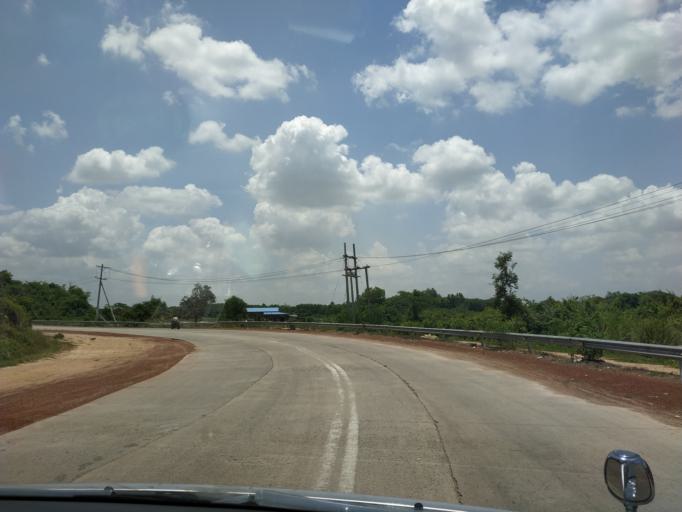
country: MM
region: Bago
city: Bago
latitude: 17.4668
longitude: 96.4604
